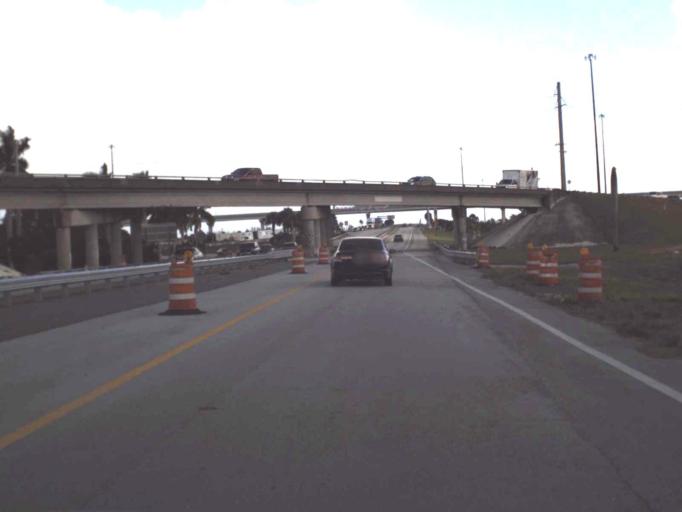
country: US
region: Florida
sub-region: Miami-Dade County
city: Norland
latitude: 25.9324
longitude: -80.2132
